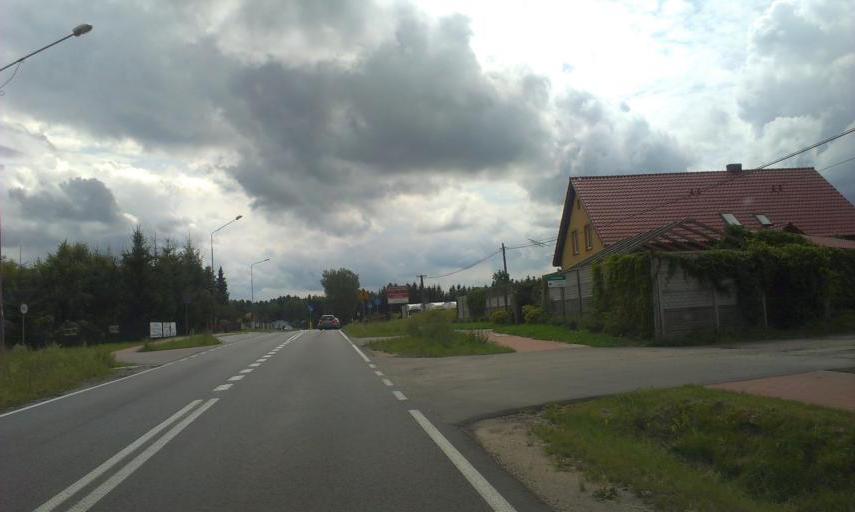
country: PL
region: West Pomeranian Voivodeship
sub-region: Koszalin
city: Koszalin
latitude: 54.1465
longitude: 16.1739
